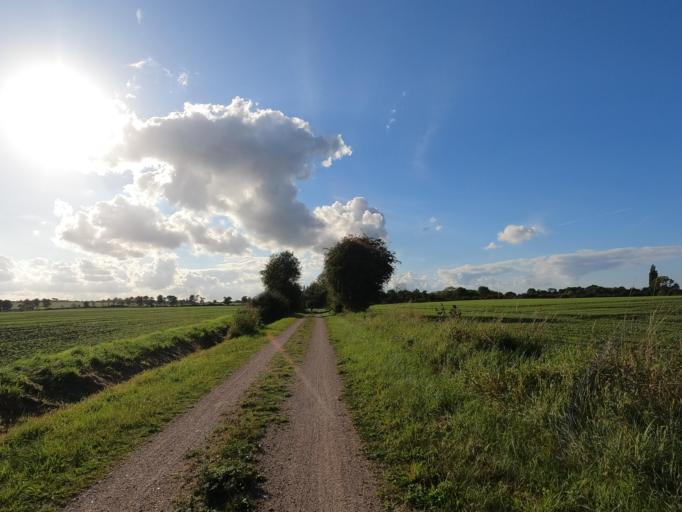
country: DE
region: Schleswig-Holstein
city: Grossenbrode
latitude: 54.3582
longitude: 11.0498
